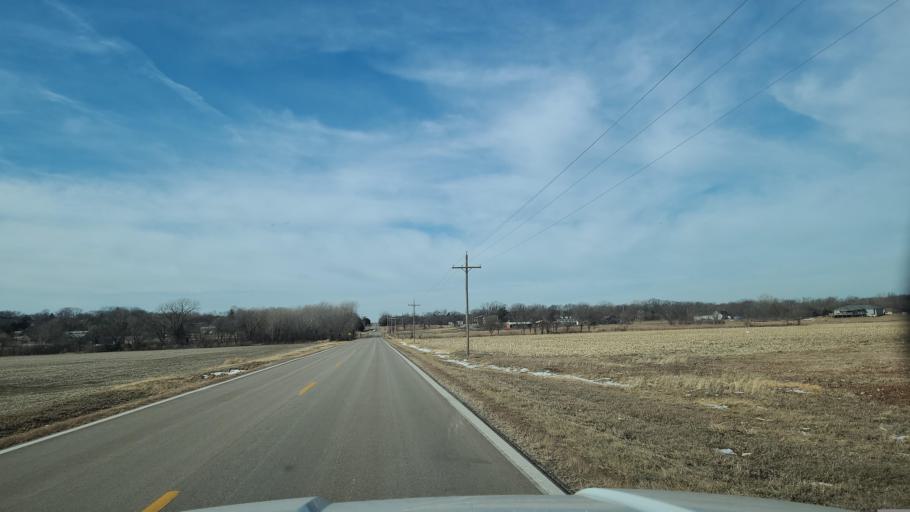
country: US
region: Kansas
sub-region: Douglas County
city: Lawrence
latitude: 38.8845
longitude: -95.1990
